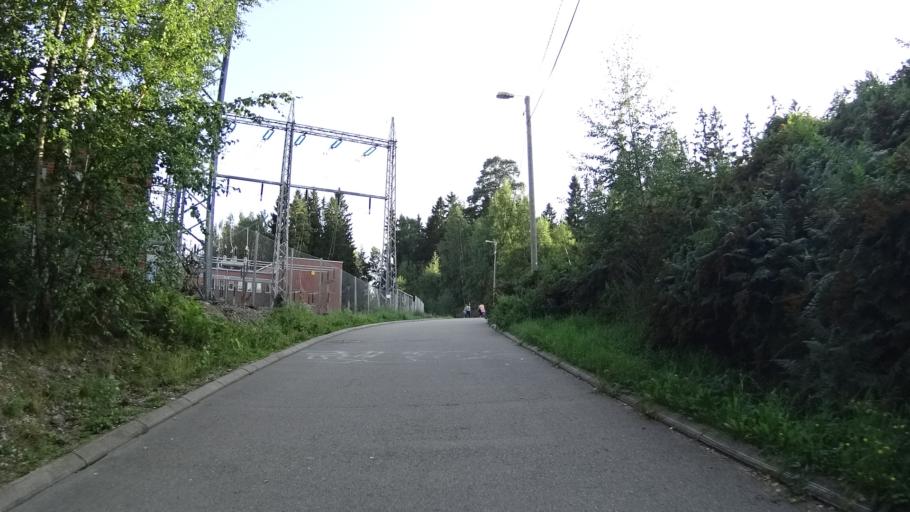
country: FI
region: Uusimaa
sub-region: Helsinki
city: Teekkarikylae
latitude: 60.2560
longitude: 24.8554
